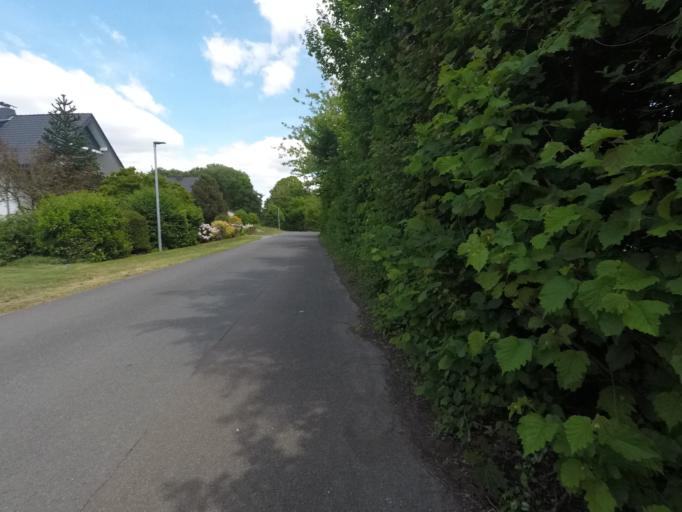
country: DE
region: North Rhine-Westphalia
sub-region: Regierungsbezirk Detmold
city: Rodinghausen
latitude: 52.2496
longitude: 8.4727
